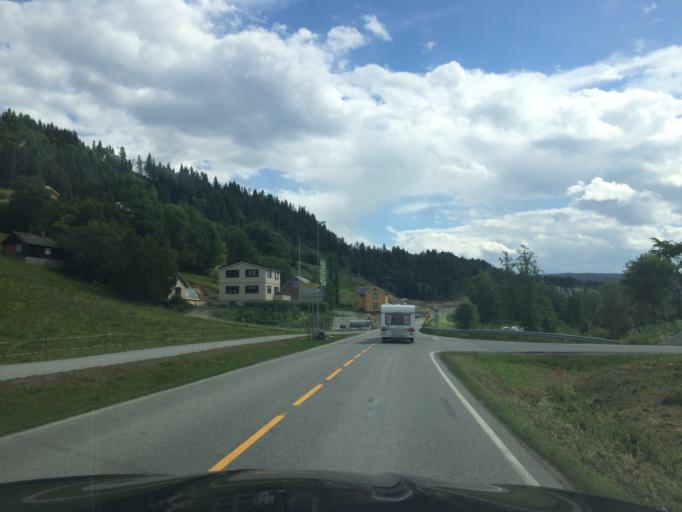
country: NO
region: Sor-Trondelag
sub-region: Selbu
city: Mebonden
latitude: 63.2172
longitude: 11.0442
